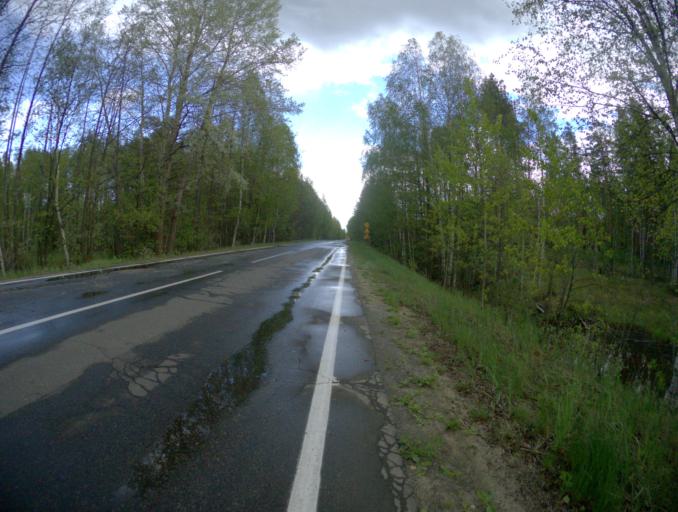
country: RU
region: Vladimir
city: Mezinovskiy
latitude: 55.5951
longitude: 40.3842
